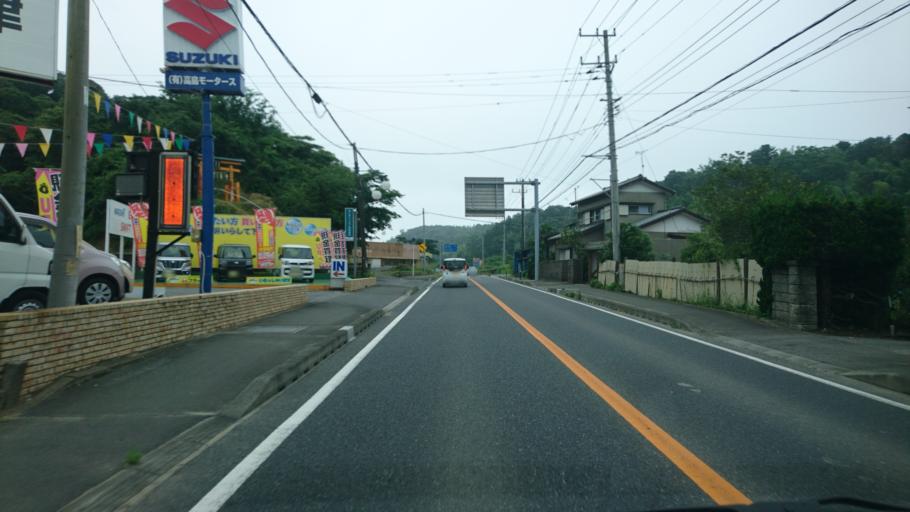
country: JP
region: Chiba
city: Kimitsu
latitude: 35.2595
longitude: 139.8844
